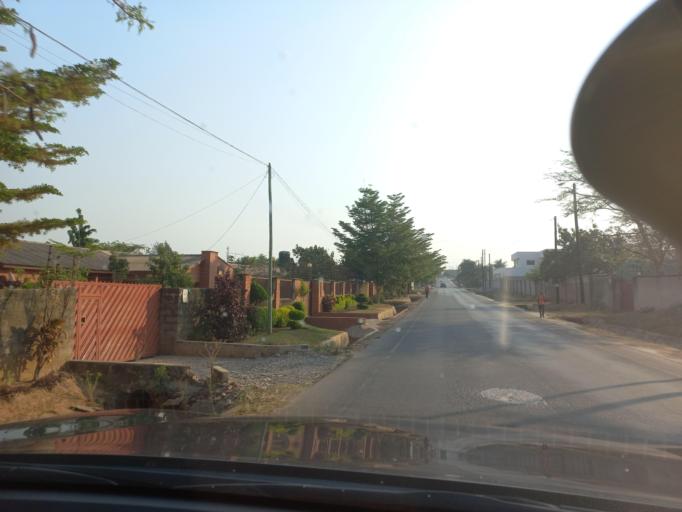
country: ZM
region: Lusaka
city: Lusaka
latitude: -15.4237
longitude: 28.3628
